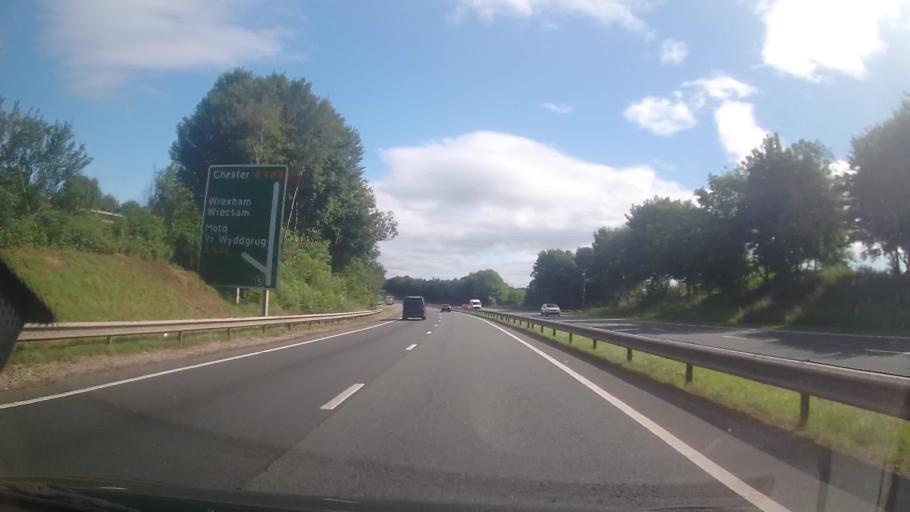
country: GB
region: Wales
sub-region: Wrexham
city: Wrexham
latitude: 53.0509
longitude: -3.0169
